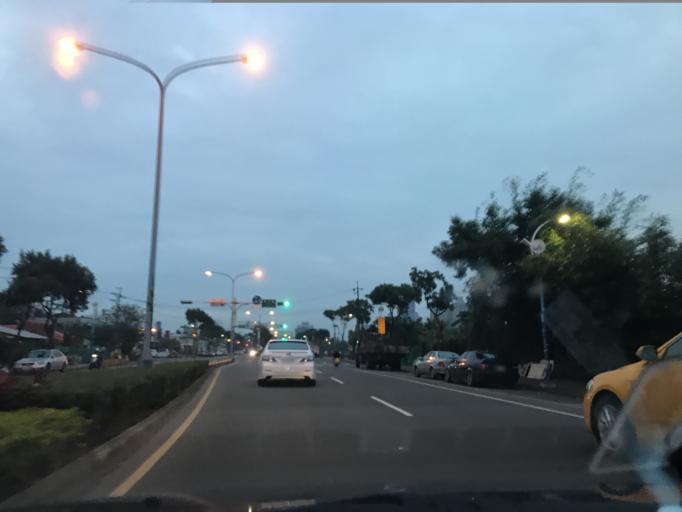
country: TW
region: Taiwan
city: Daxi
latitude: 24.9357
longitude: 121.2393
